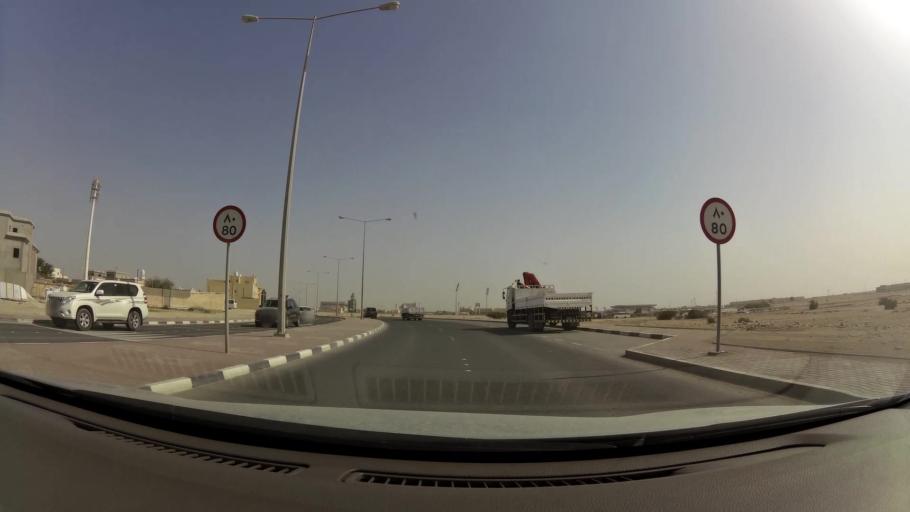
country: QA
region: Baladiyat ar Rayyan
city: Ar Rayyan
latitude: 25.3533
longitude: 51.4381
